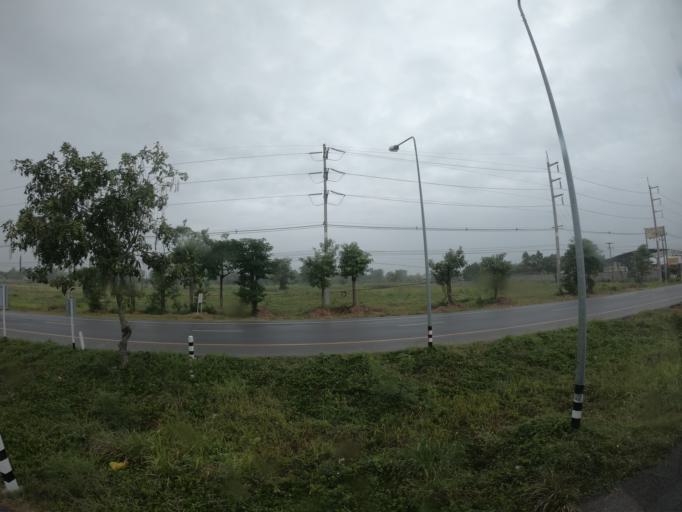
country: TH
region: Maha Sarakham
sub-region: Amphoe Borabue
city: Borabue
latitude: 16.0493
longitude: 103.0964
